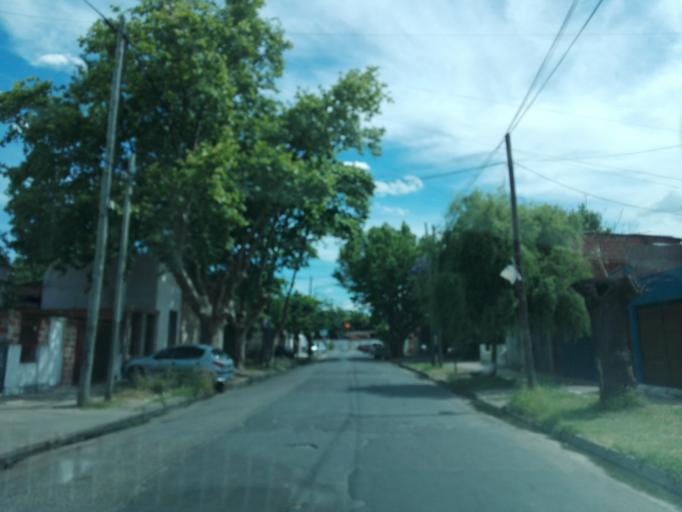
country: AR
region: Buenos Aires
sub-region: Partido de Lanus
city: Lanus
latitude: -34.7246
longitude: -58.3895
